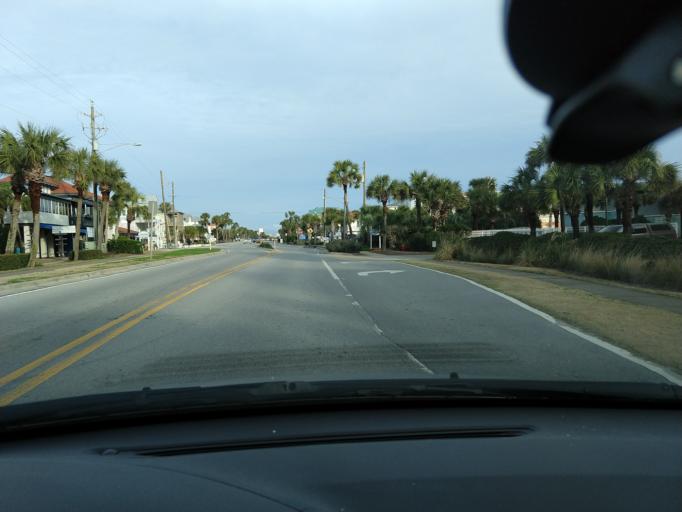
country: US
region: Florida
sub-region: Walton County
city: Miramar Beach
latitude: 30.3828
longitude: -86.4272
